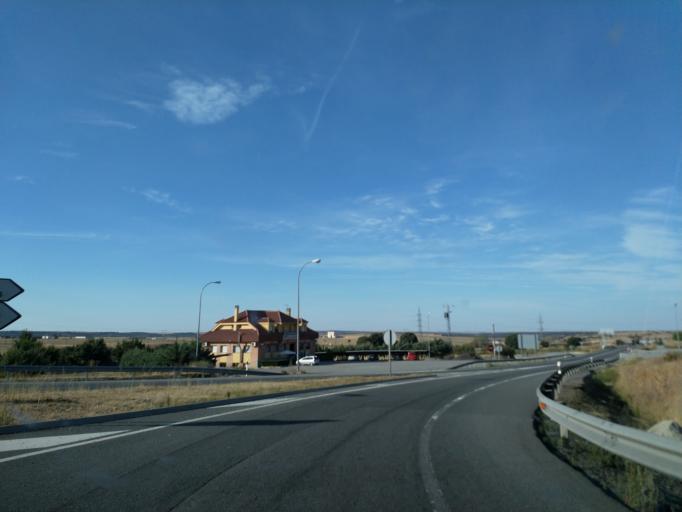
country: ES
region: Castille and Leon
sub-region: Provincia de Segovia
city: Villacastin
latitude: 40.7773
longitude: -4.4230
